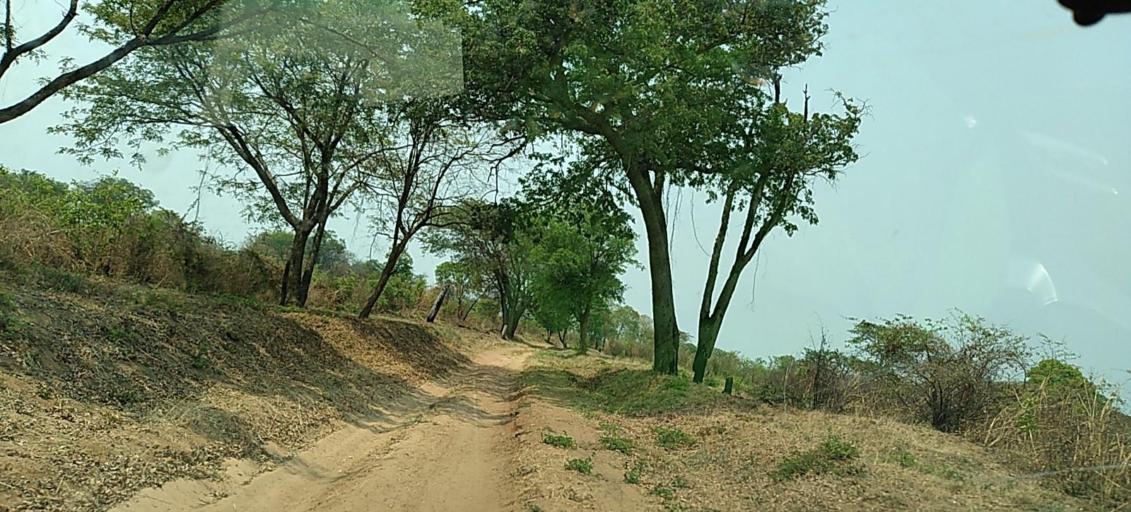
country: ZM
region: Western
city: Lukulu
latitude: -13.9710
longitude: 23.2302
